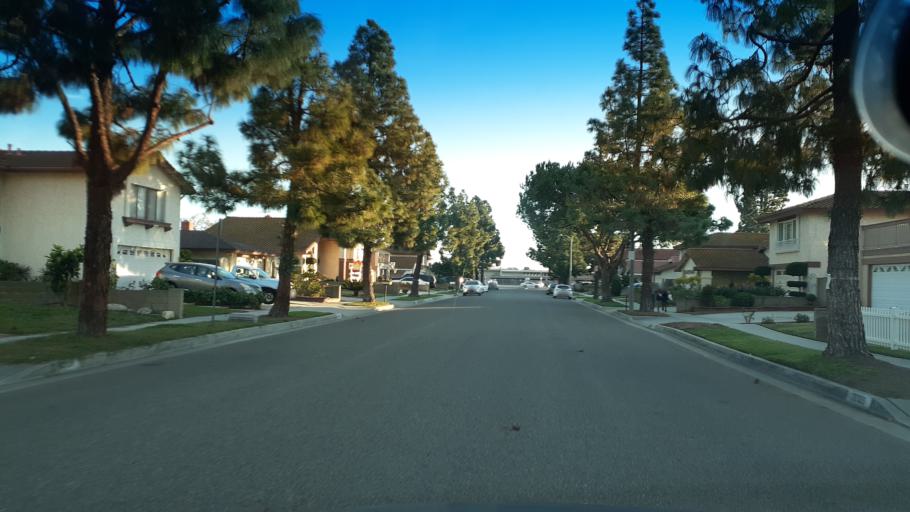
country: US
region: California
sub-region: Los Angeles County
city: Cerritos
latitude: 33.8478
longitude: -118.0745
